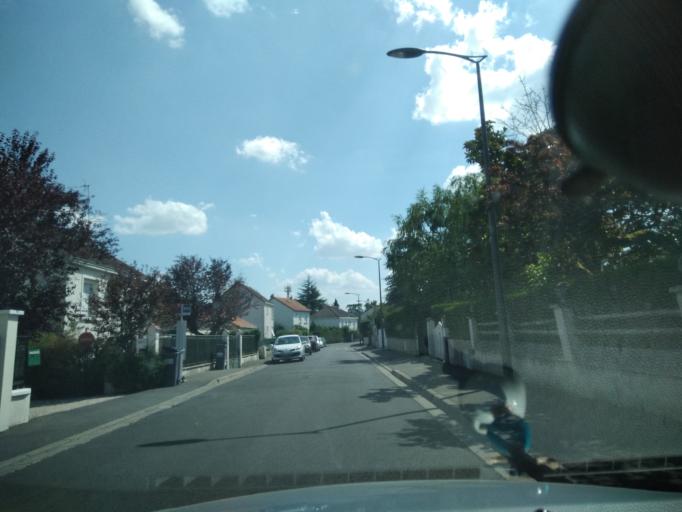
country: FR
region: Centre
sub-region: Departement d'Indre-et-Loire
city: Chambray-les-Tours
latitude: 47.3506
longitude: 0.6926
